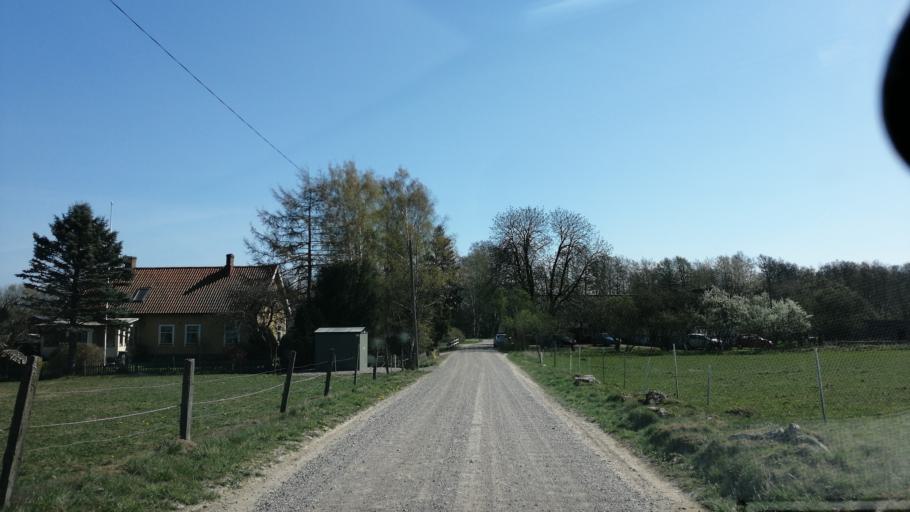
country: SE
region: Skane
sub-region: Astorps Kommun
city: Kvidinge
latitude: 56.1147
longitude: 13.0367
